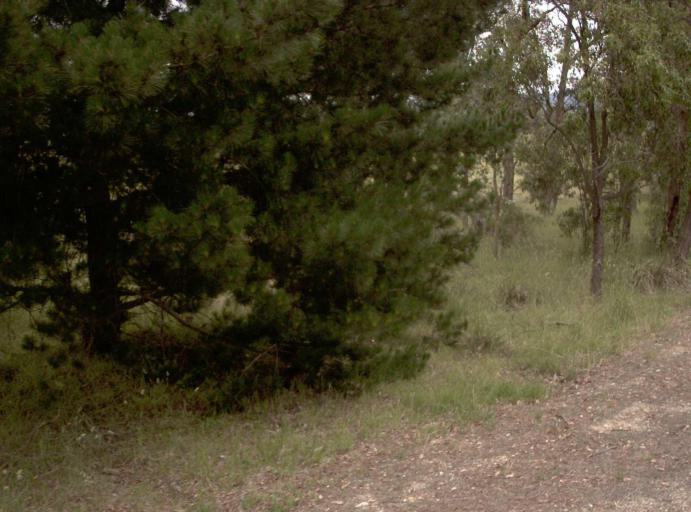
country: AU
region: Victoria
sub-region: East Gippsland
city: Bairnsdale
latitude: -37.7905
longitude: 147.3267
